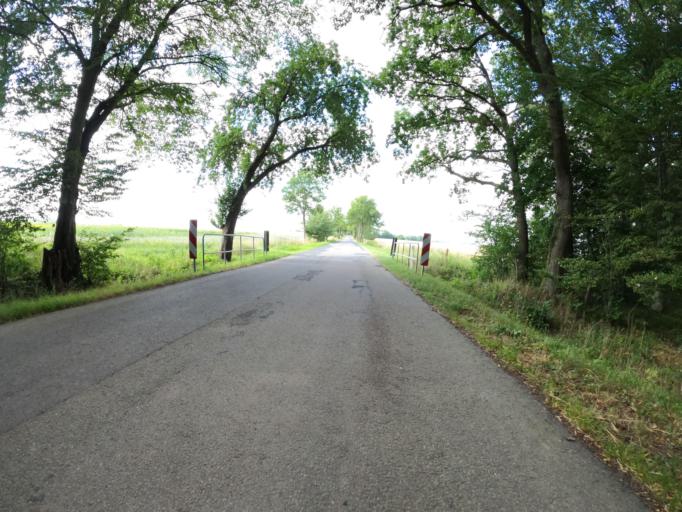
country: DE
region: Mecklenburg-Vorpommern
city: Woldegk
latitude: 53.4315
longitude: 13.6010
